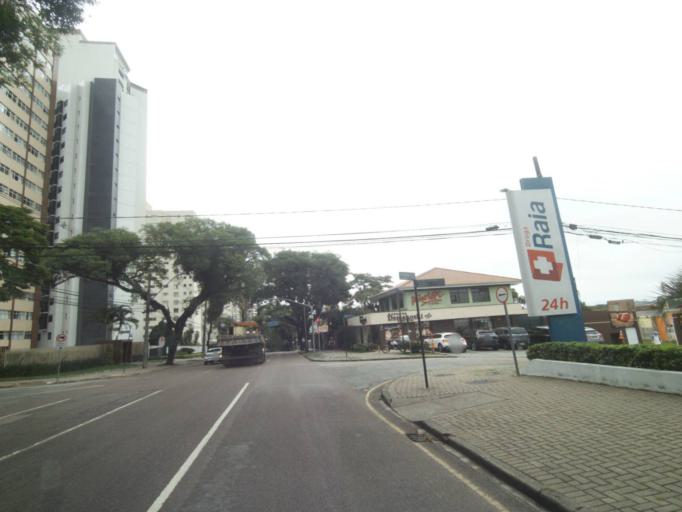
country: BR
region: Parana
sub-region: Curitiba
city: Curitiba
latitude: -25.4296
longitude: -49.2947
